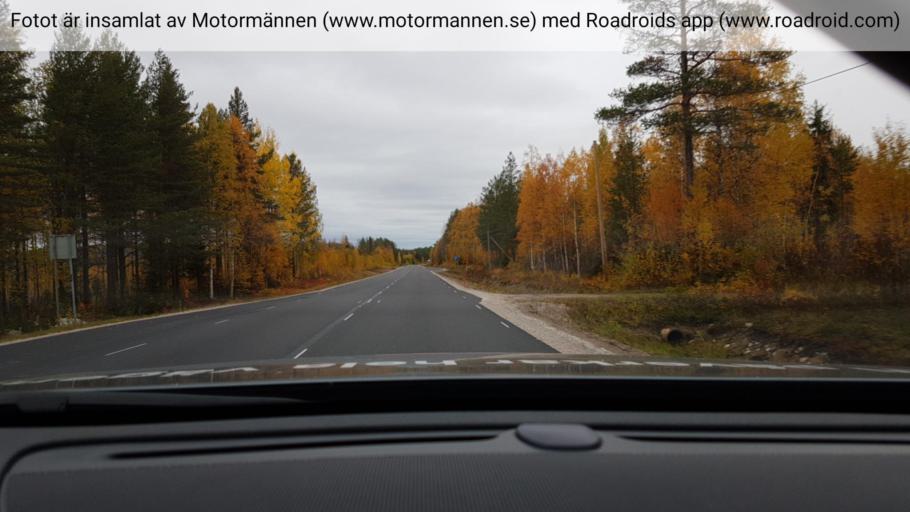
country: SE
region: Norrbotten
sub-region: Overkalix Kommun
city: OEverkalix
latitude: 66.3804
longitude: 22.8331
